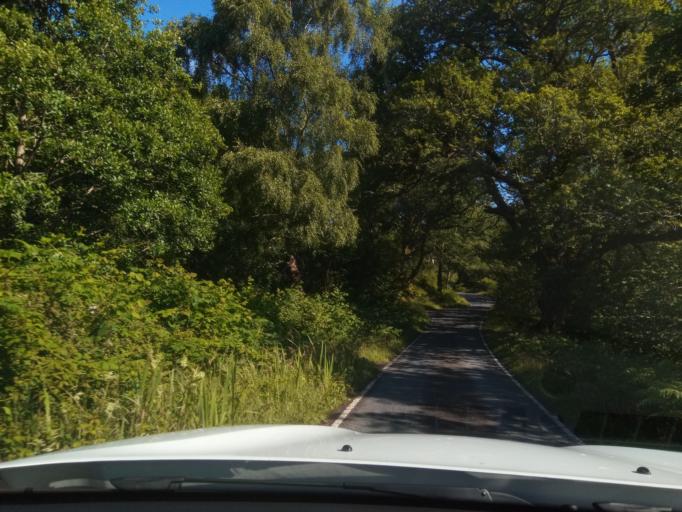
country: GB
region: Scotland
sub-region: Argyll and Bute
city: Isle Of Mull
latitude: 56.6906
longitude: -5.6686
